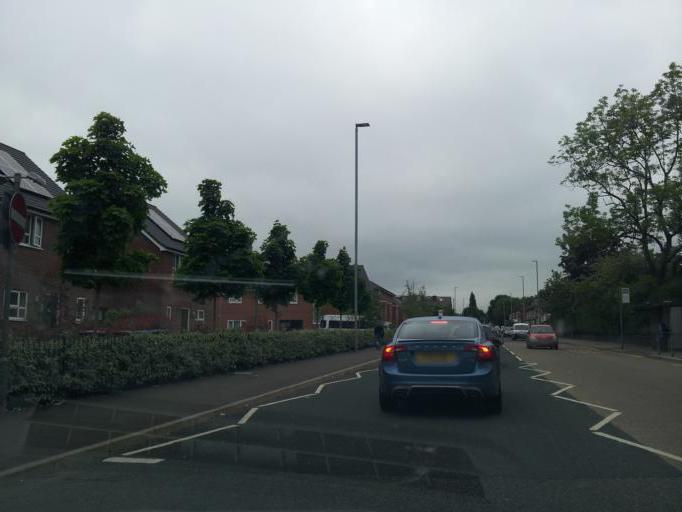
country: GB
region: England
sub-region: Manchester
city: Crumpsall
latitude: 53.5056
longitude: -2.2542
